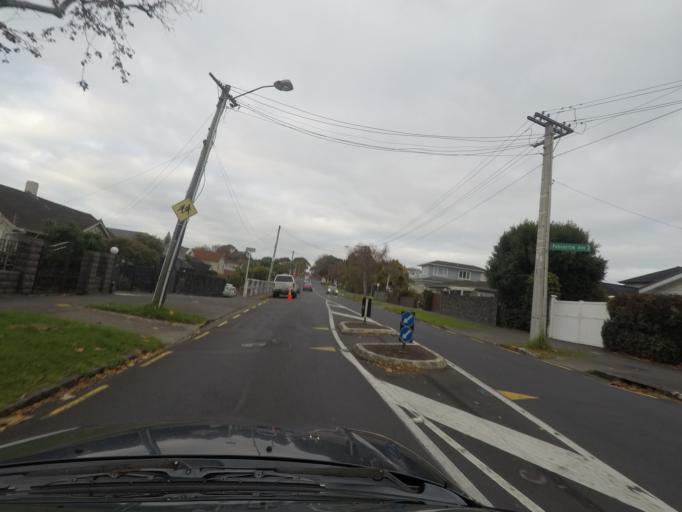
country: NZ
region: Auckland
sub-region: Auckland
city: Auckland
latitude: -36.8894
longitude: 174.7667
